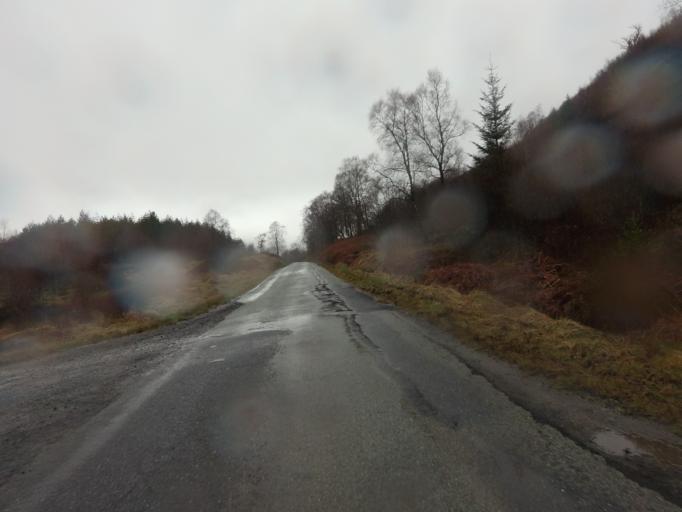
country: GB
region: Scotland
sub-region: West Dunbartonshire
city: Balloch
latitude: 56.2418
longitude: -4.5702
